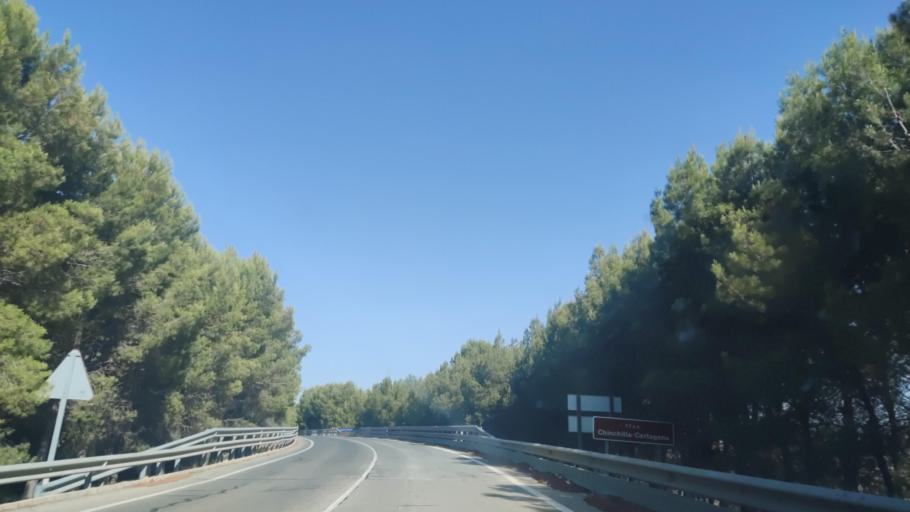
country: ES
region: Castille-La Mancha
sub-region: Provincia de Albacete
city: Hellin
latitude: 38.4775
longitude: -1.6037
